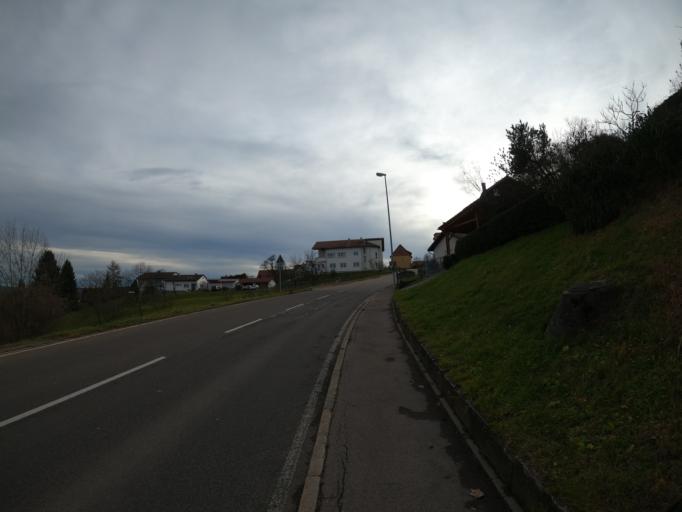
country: DE
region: Baden-Wuerttemberg
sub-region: Regierungsbezirk Stuttgart
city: Ottenbach
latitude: 48.7431
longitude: 9.7221
